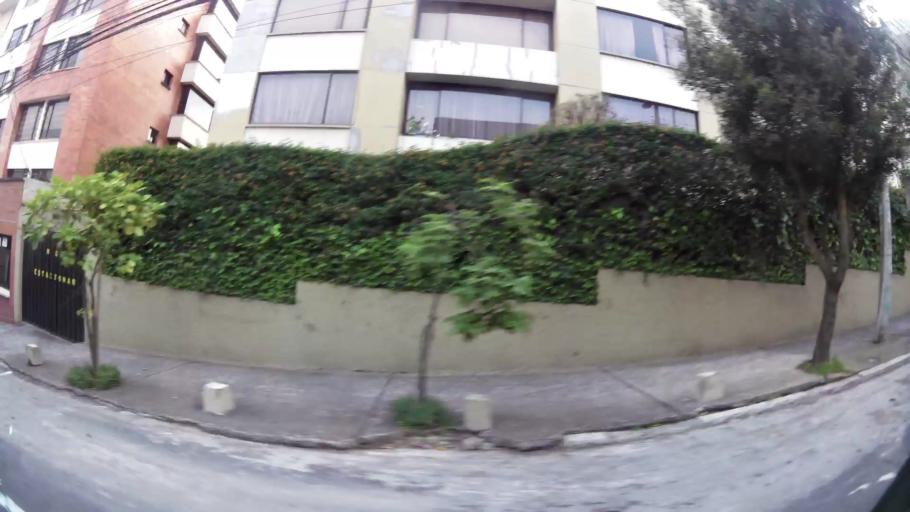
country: EC
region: Pichincha
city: Quito
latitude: -0.2006
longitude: -78.4847
